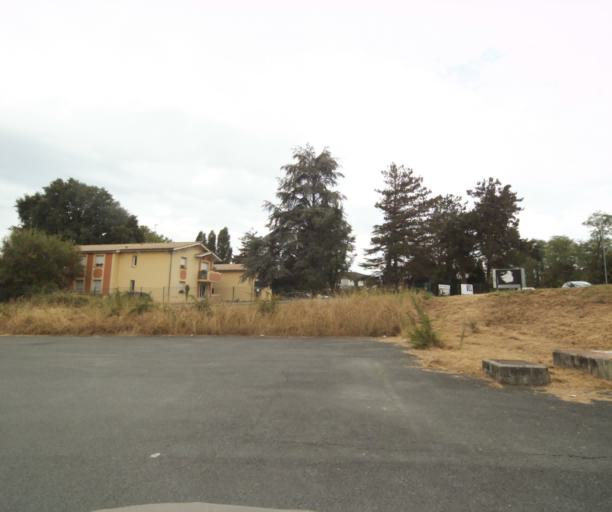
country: FR
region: Aquitaine
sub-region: Departement de la Gironde
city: Creon
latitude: 44.7718
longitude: -0.3417
